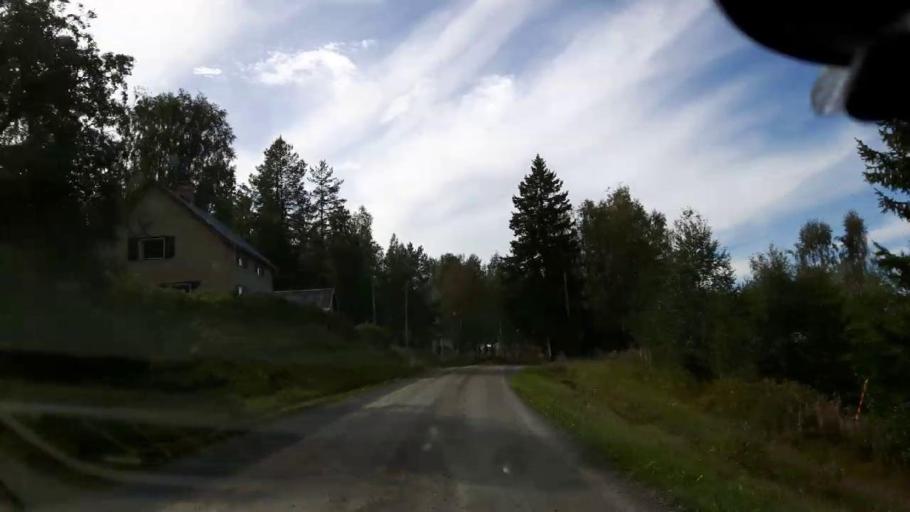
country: SE
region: Jaemtland
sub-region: Ragunda Kommun
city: Hammarstrand
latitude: 63.1374
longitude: 16.1881
